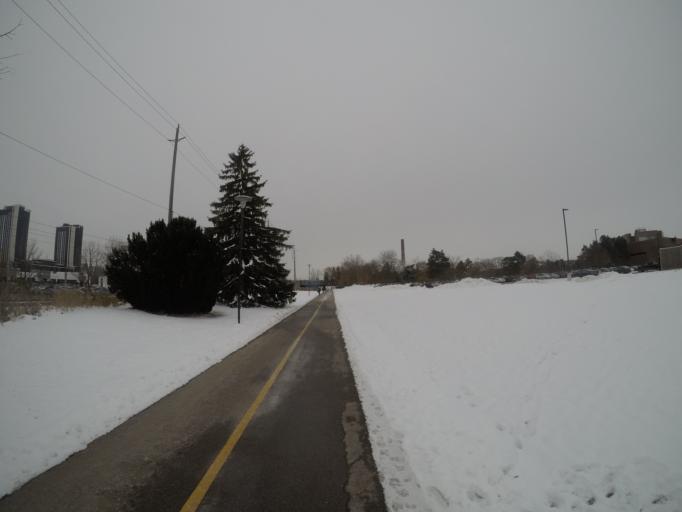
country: CA
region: Ontario
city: Waterloo
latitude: 43.4774
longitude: -80.5439
